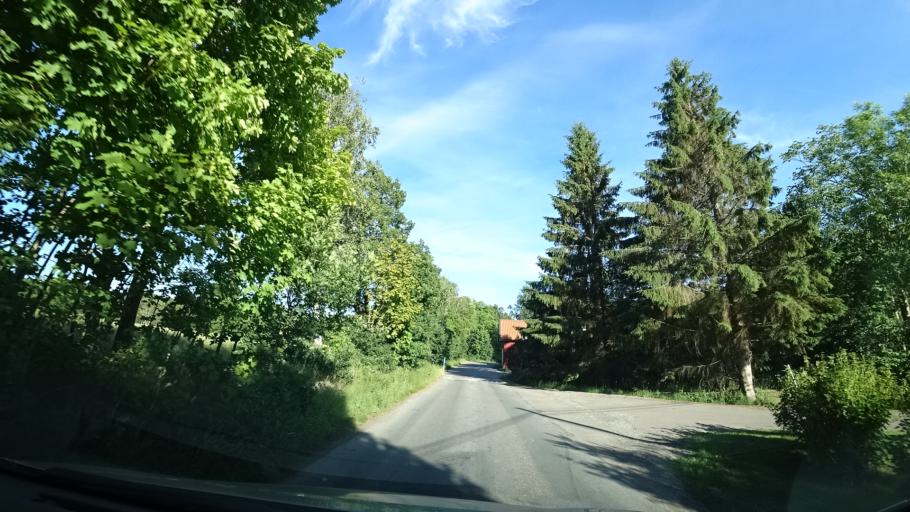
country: SE
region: Vaestra Goetaland
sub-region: Goteborg
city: Billdal
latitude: 57.5765
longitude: 11.9640
